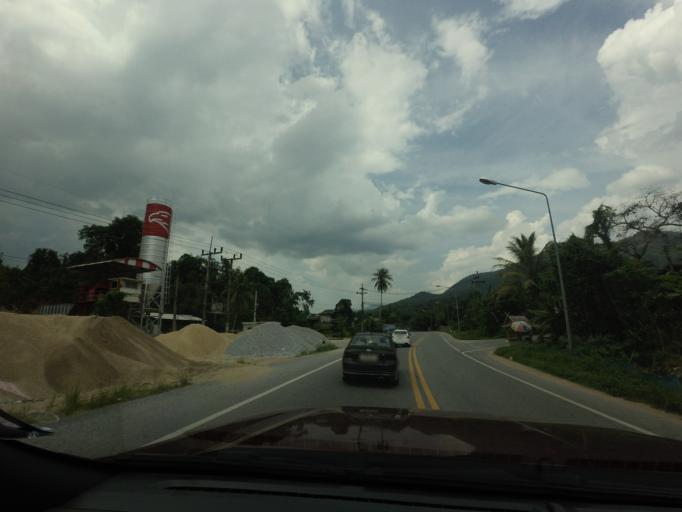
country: TH
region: Yala
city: Ban Nang Sata
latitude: 6.2803
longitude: 101.2918
